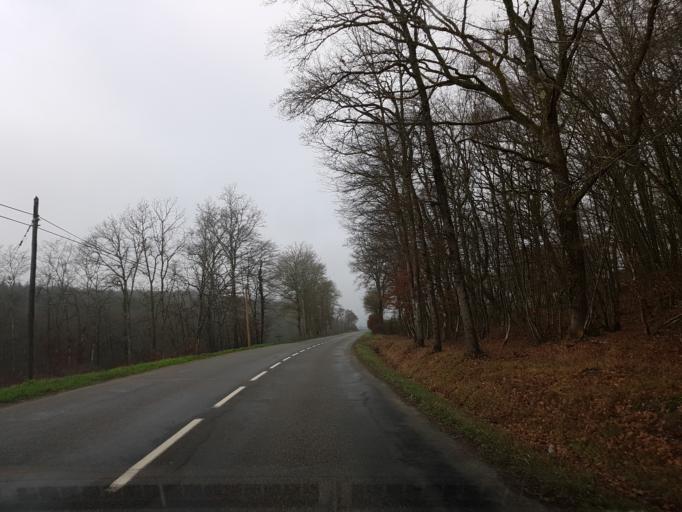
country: FR
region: Bourgogne
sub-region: Departement de Saone-et-Loire
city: Toulon-sur-Arroux
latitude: 46.6856
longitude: 4.1688
